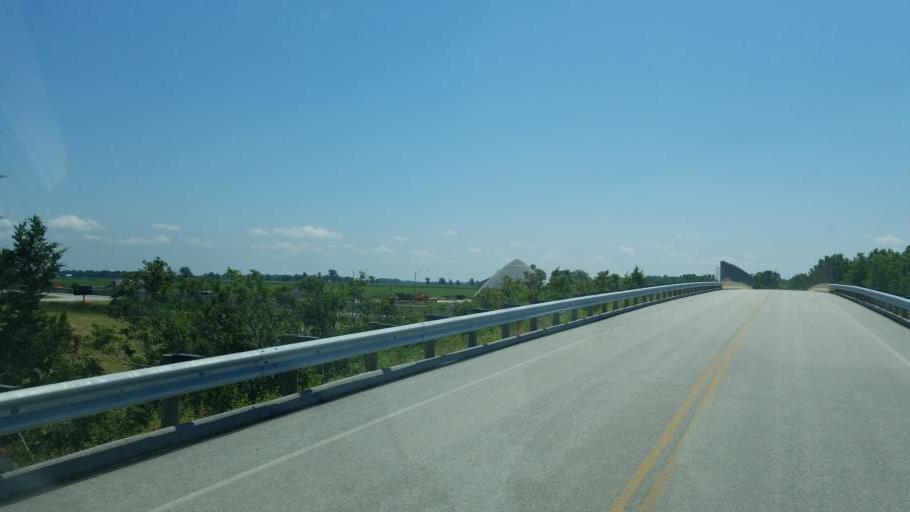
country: US
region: Ohio
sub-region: Sandusky County
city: Fremont
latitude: 41.3957
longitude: -83.0873
